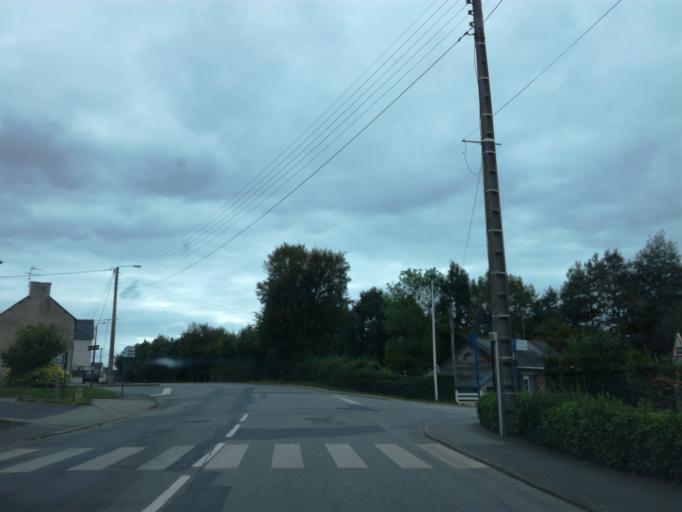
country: FR
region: Brittany
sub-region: Departement des Cotes-d'Armor
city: Loudeac
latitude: 48.1710
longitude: -2.7543
